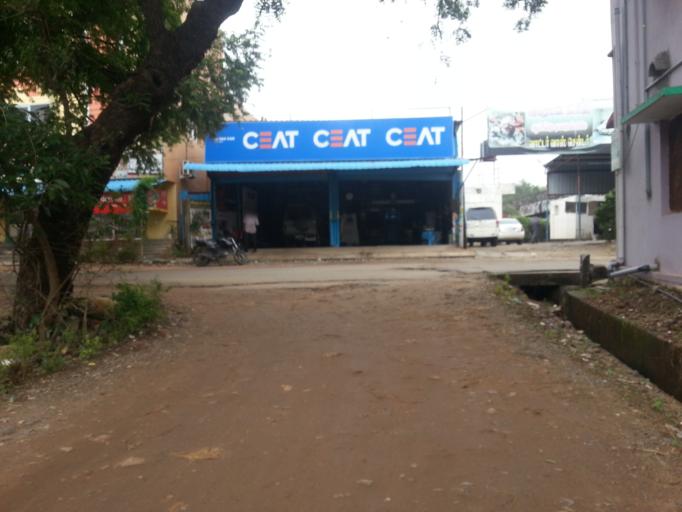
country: IN
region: Tamil Nadu
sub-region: Perambalur
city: Perambalur
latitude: 11.2403
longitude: 78.8626
